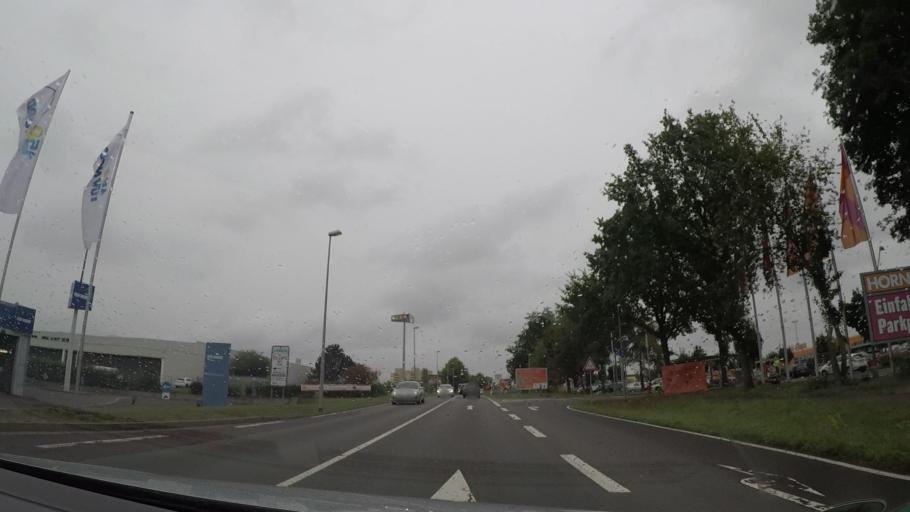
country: DE
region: Saxony-Anhalt
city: Neue Neustadt
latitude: 52.1681
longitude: 11.6055
